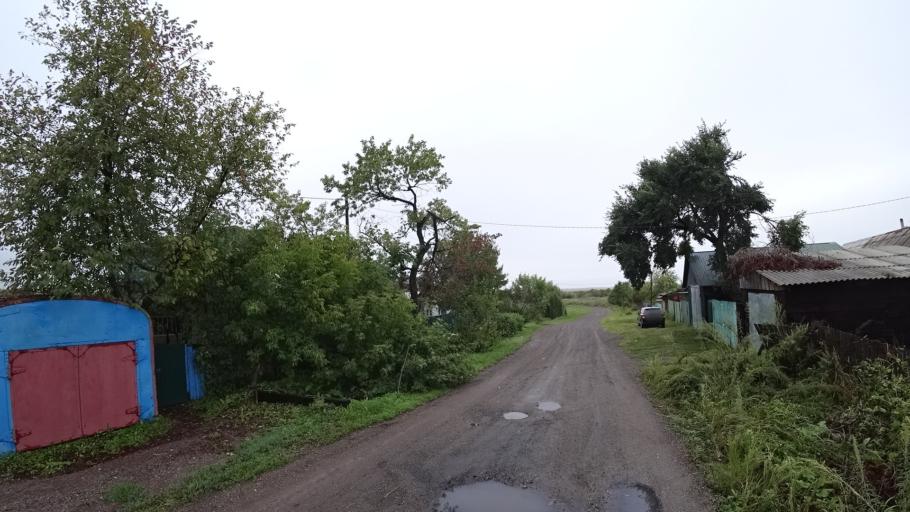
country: RU
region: Primorskiy
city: Monastyrishche
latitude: 44.1915
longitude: 132.4189
